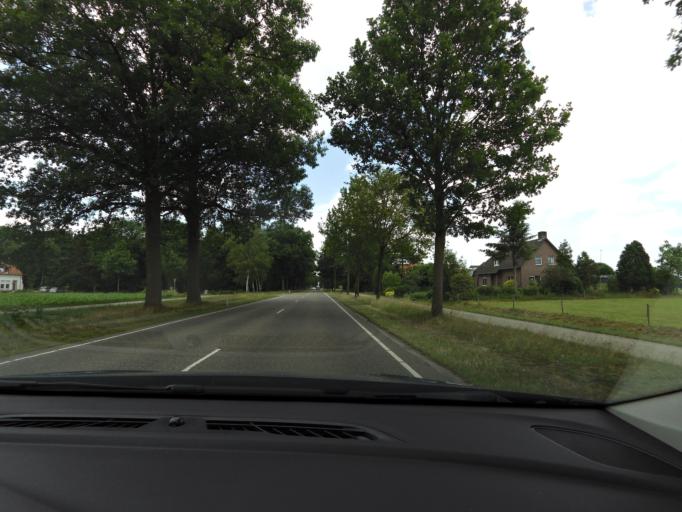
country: NL
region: North Brabant
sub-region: Gemeente Baarle-Nassau
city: Baarle-Nassau
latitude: 51.4665
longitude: 4.9046
